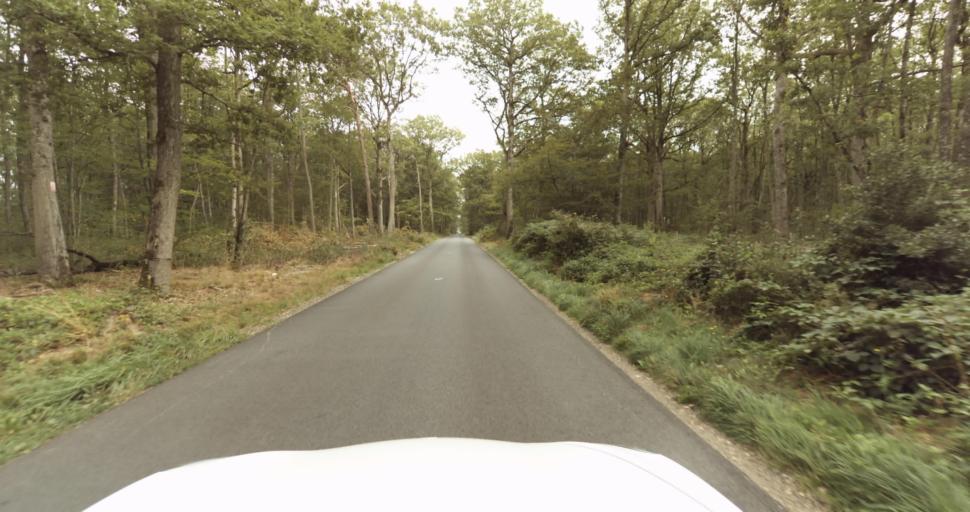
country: FR
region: Haute-Normandie
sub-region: Departement de l'Eure
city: Saint-Sebastien-de-Morsent
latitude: 48.9802
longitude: 1.0747
